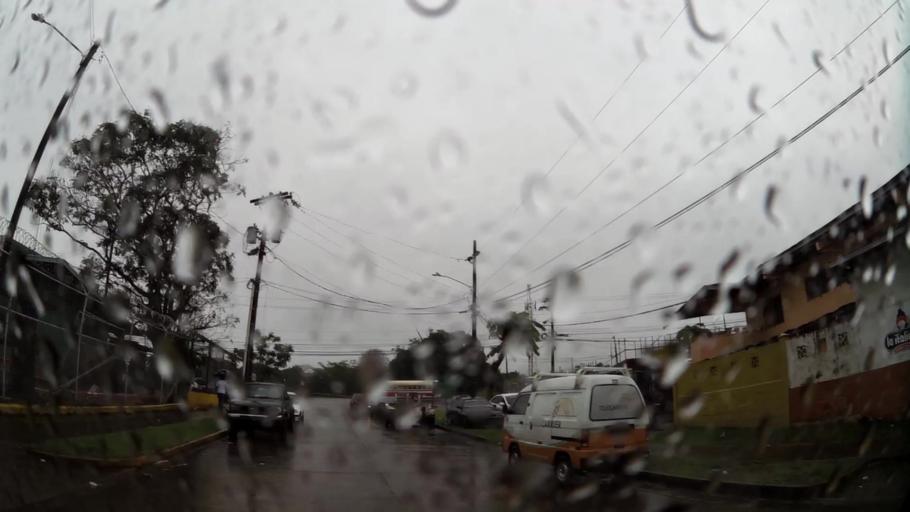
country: PA
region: Colon
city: Sabanitas
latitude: 9.3441
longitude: -79.8057
